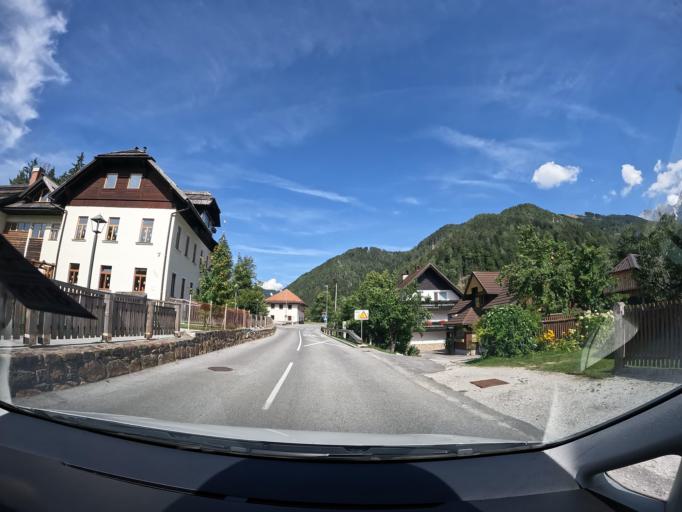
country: AT
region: Carinthia
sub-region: Politischer Bezirk Klagenfurt Land
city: Moosburg
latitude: 46.6710
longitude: 14.1252
